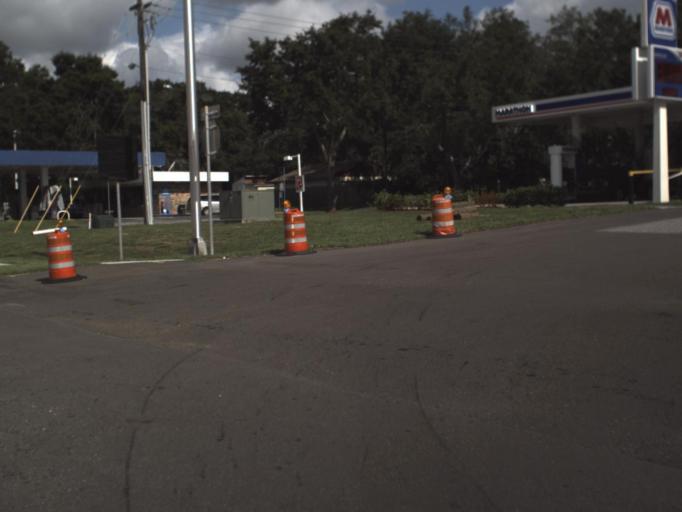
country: US
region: Florida
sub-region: Hillsborough County
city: Temple Terrace
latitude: 28.0545
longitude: -82.3682
